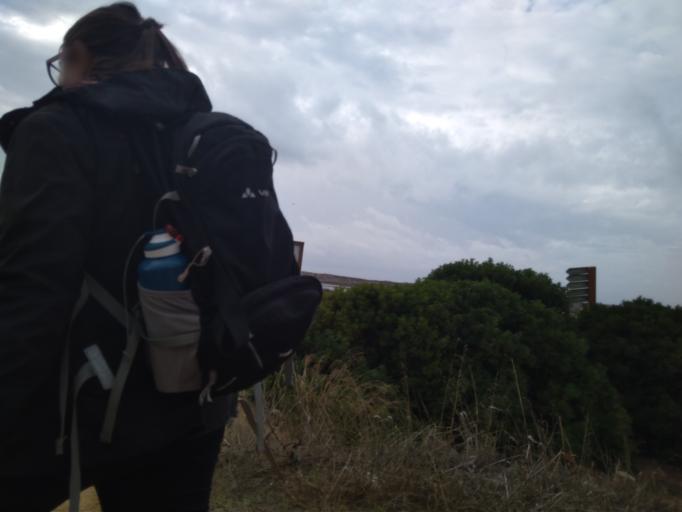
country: PT
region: Faro
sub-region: Loule
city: Almancil
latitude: 37.0247
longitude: -8.0152
